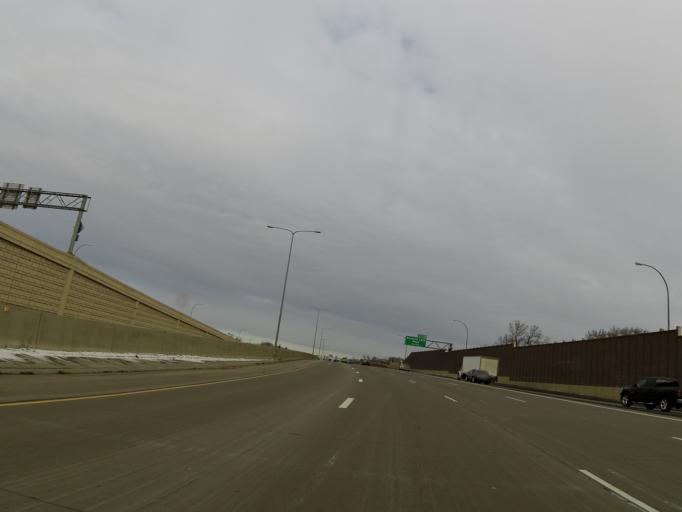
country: US
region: Minnesota
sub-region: Hennepin County
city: Richfield
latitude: 44.8924
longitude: -93.2749
